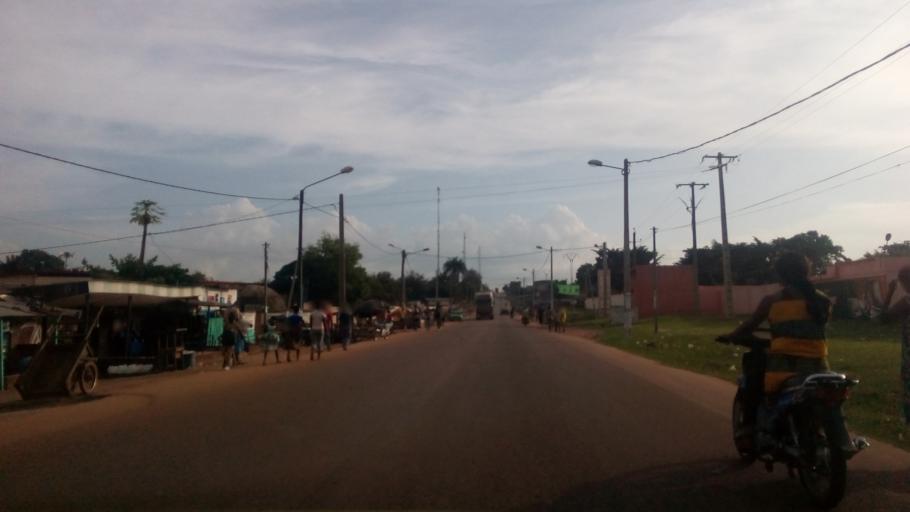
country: CI
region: Dix-Huit Montagnes
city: Duekoue
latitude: 6.7416
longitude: -7.3426
